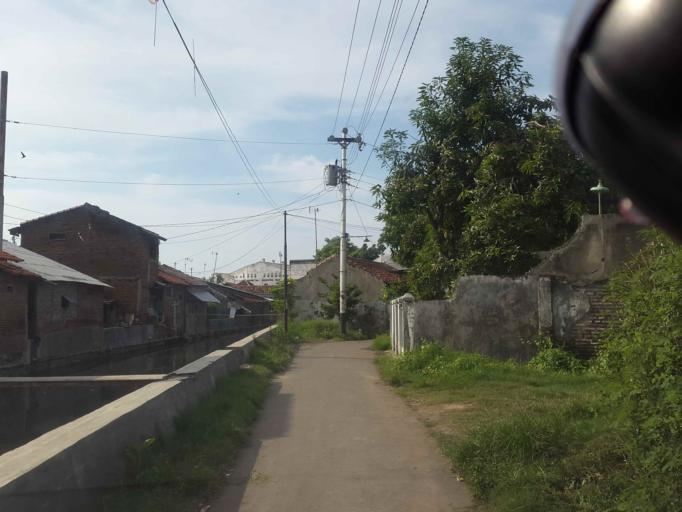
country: ID
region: Central Java
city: Tegal
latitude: -6.8572
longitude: 109.1412
